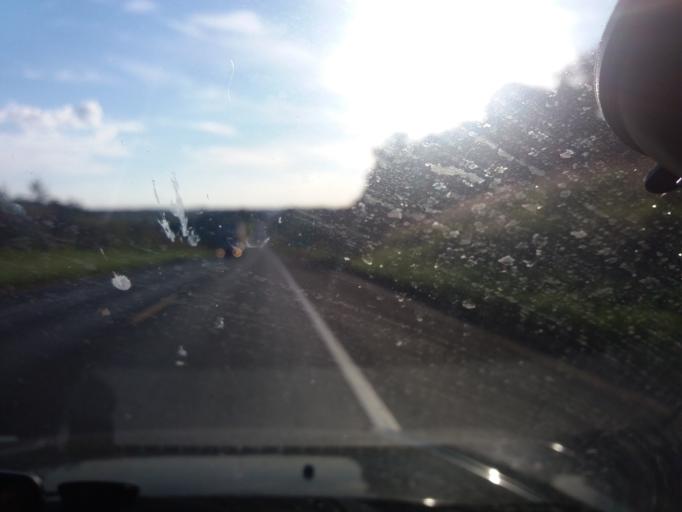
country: BR
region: Sao Paulo
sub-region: Buri
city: Buri
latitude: -23.9357
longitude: -48.6271
